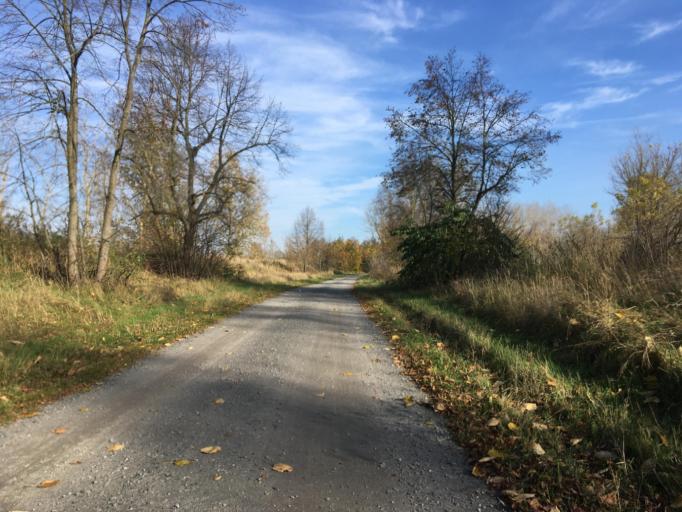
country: DE
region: Berlin
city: Buch
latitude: 52.6672
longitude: 13.4776
